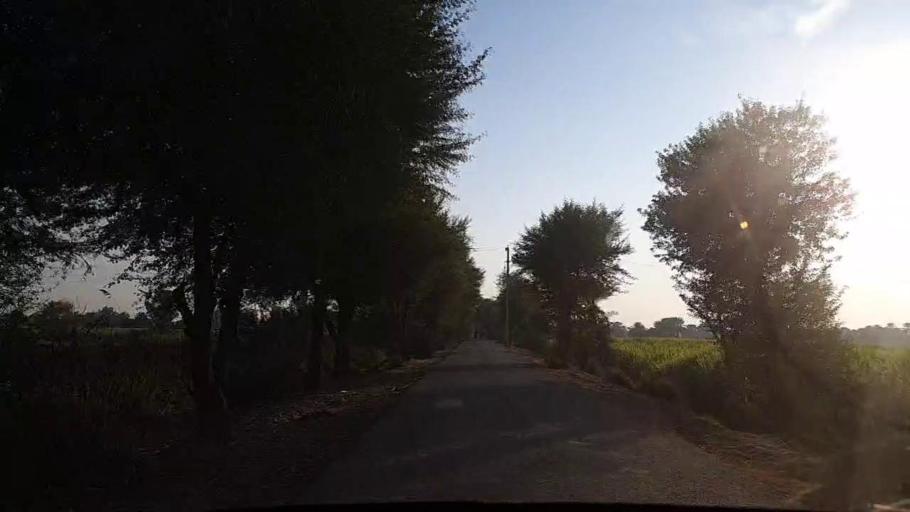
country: PK
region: Sindh
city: Sobhadero
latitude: 27.3936
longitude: 68.3857
